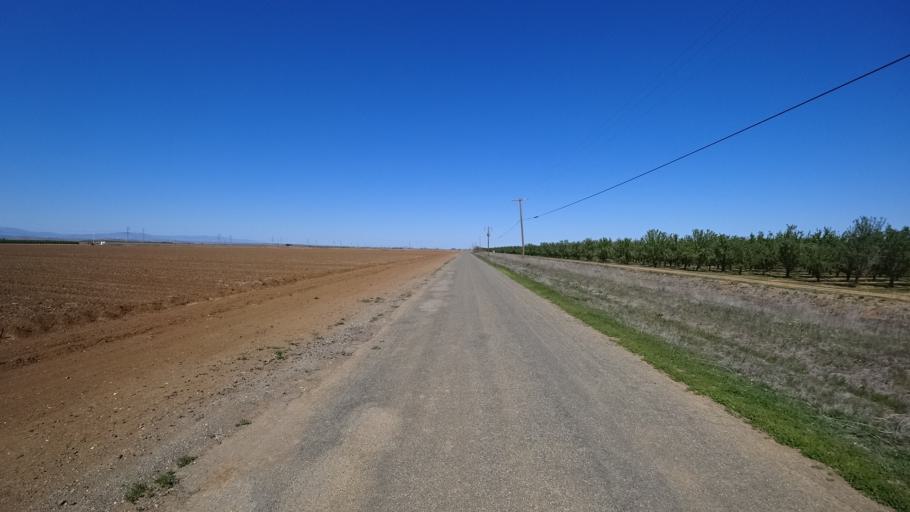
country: US
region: California
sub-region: Glenn County
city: Willows
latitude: 39.4983
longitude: -122.2773
